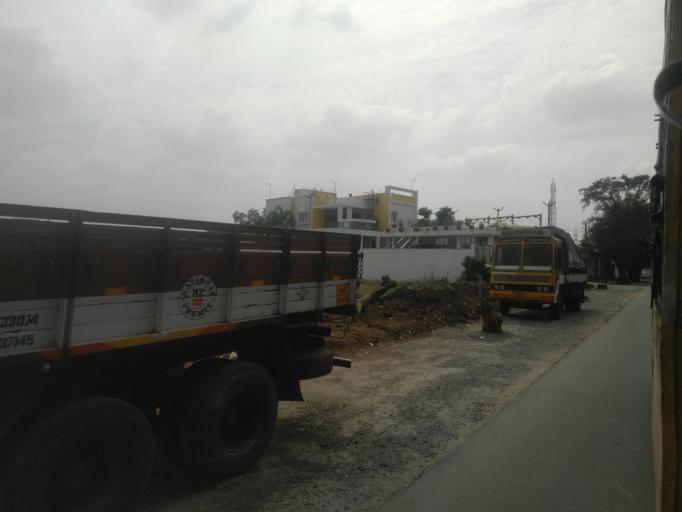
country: IN
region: Tamil Nadu
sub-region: Coimbatore
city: Irugur
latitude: 11.0115
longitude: 77.0834
